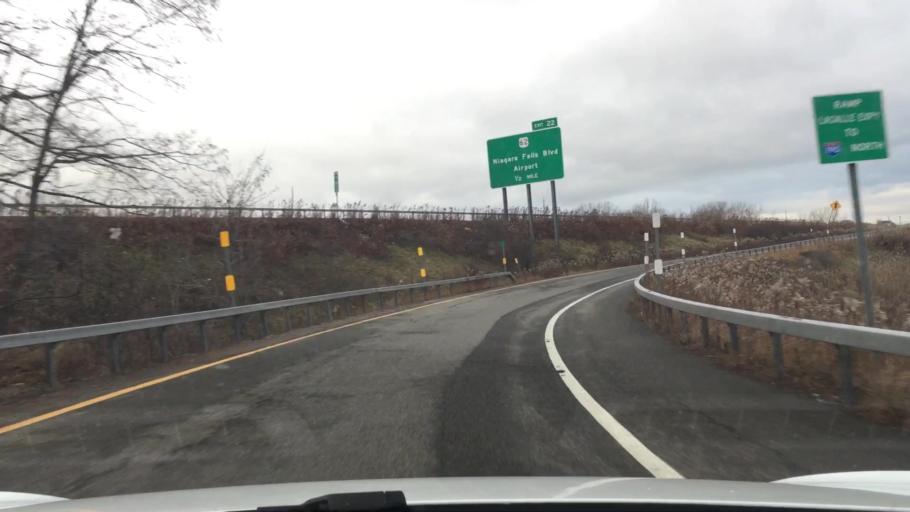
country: US
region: New York
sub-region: Niagara County
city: Niagara Falls
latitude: 43.0811
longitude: -78.9900
